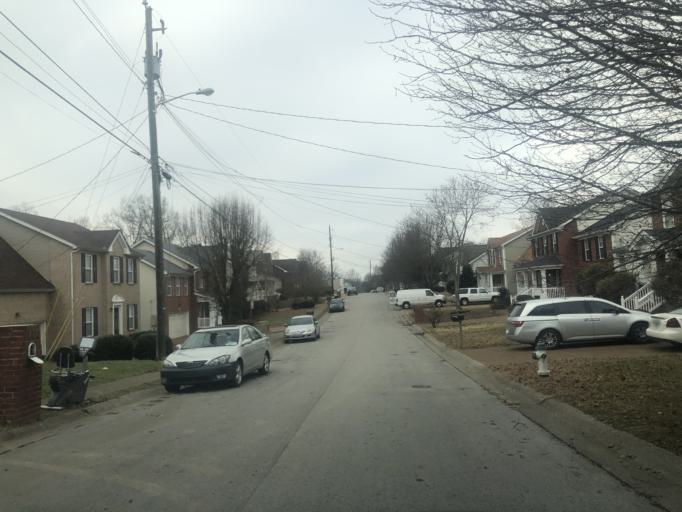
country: US
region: Tennessee
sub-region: Rutherford County
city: La Vergne
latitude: 36.0686
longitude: -86.6463
